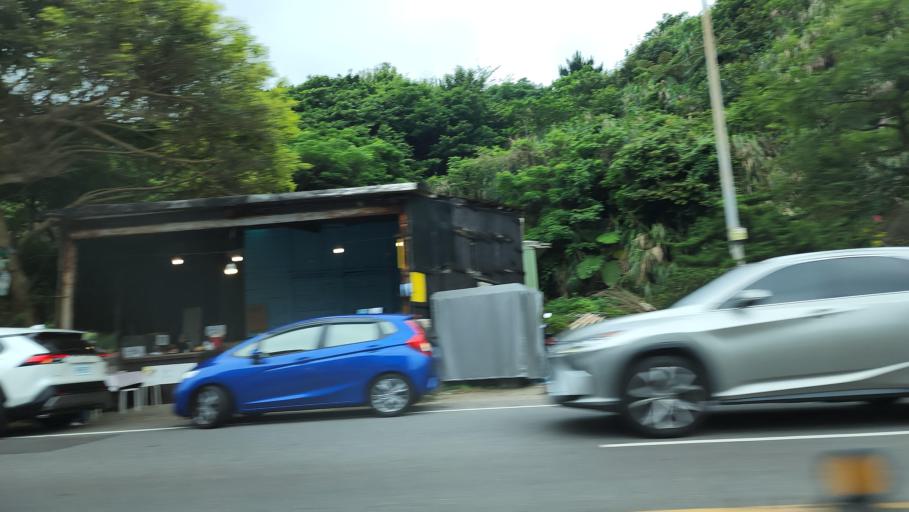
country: TW
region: Taiwan
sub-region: Keelung
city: Keelung
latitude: 25.2090
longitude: 121.6545
